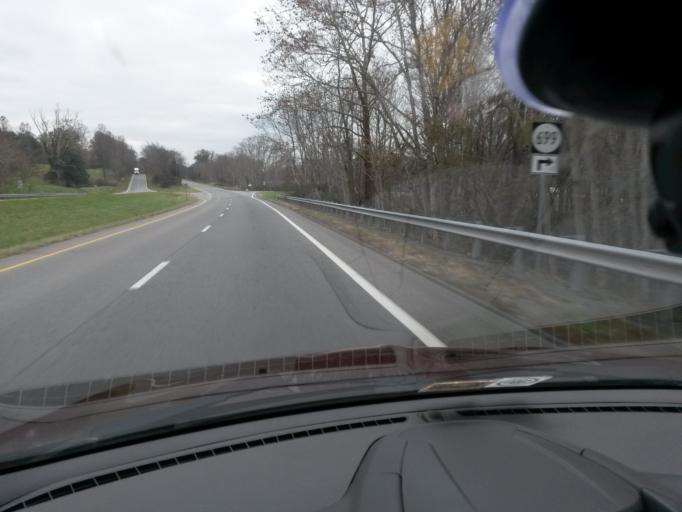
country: US
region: Virginia
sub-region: Nelson County
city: Nellysford
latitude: 37.8836
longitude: -78.7130
